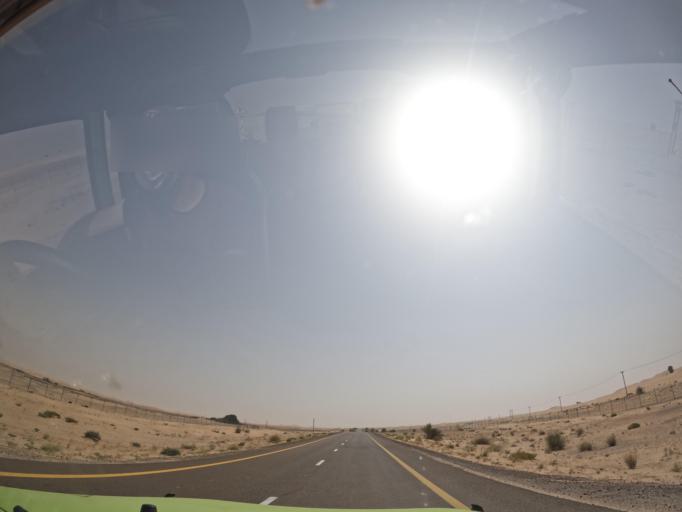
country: OM
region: Al Buraimi
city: Al Buraymi
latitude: 24.6375
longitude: 55.4889
